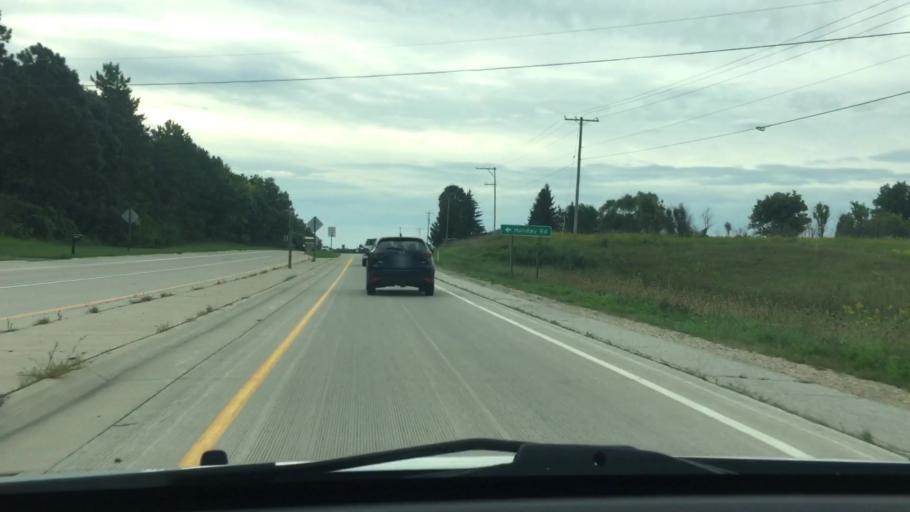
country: US
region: Wisconsin
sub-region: Waukesha County
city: North Prairie
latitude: 42.9489
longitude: -88.3532
